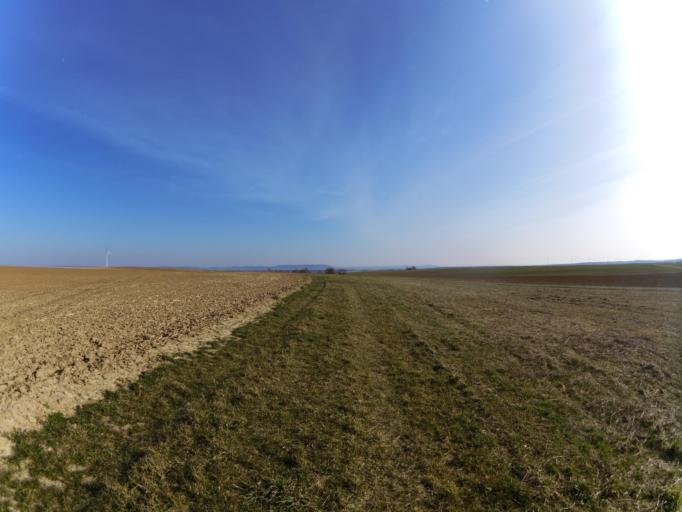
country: DE
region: Bavaria
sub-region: Regierungsbezirk Unterfranken
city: Prosselsheim
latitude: 49.8372
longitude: 10.1224
